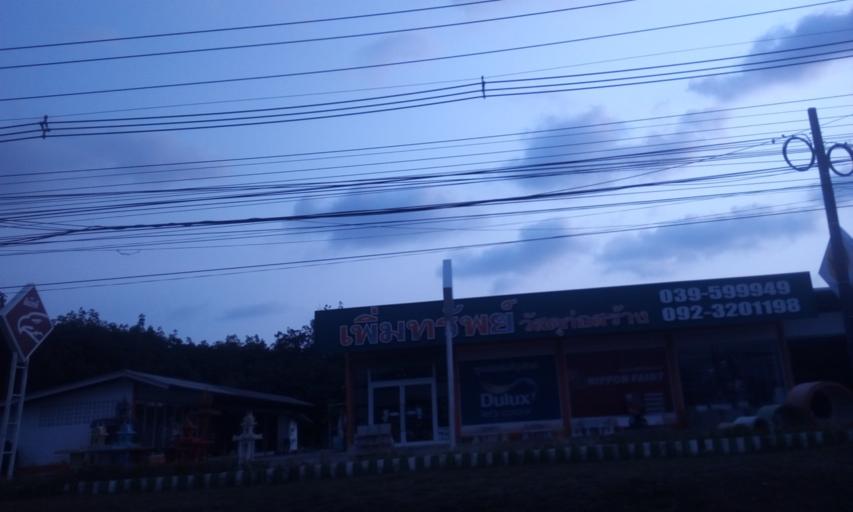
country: TH
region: Trat
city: Khao Saming
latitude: 12.3696
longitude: 102.3906
